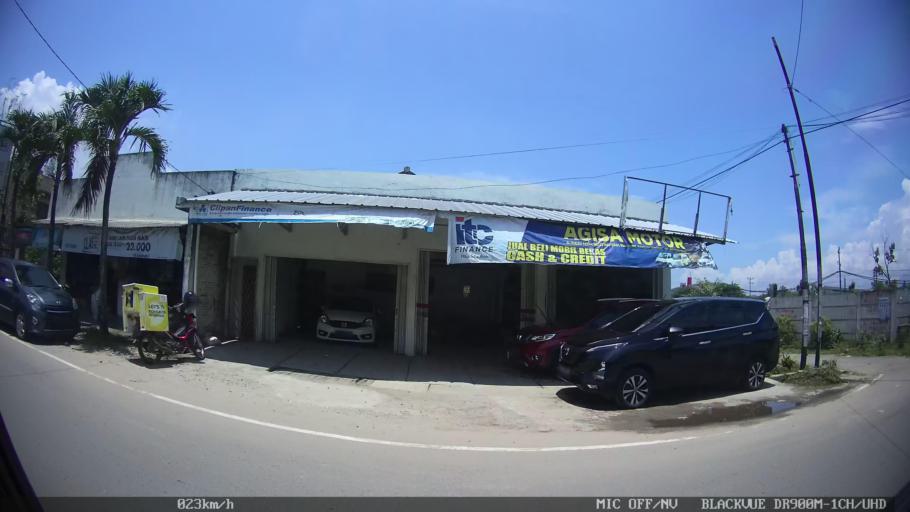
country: ID
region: Lampung
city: Kedaton
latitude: -5.3839
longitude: 105.2871
